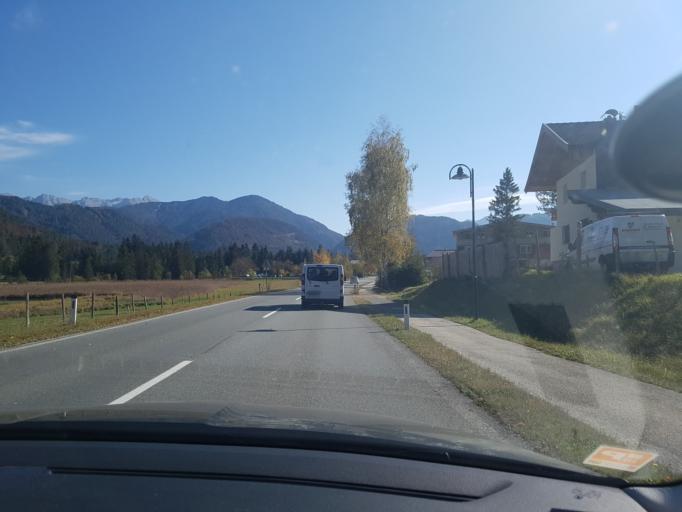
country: AT
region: Tyrol
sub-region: Politischer Bezirk Kitzbuhel
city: Waidring
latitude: 47.5322
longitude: 12.5710
